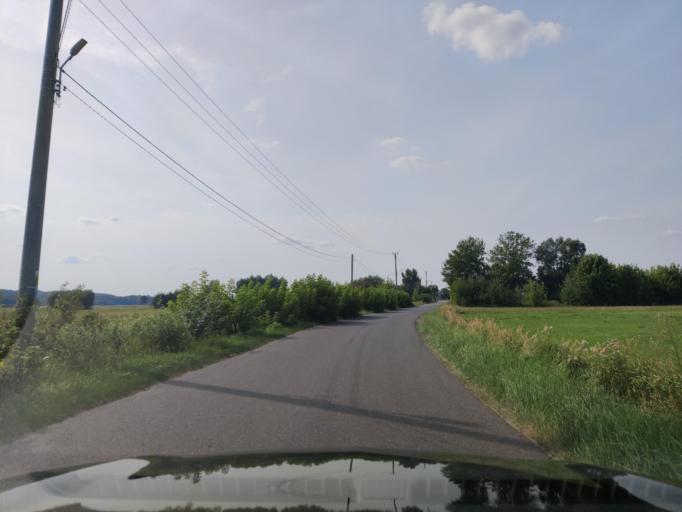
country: PL
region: Masovian Voivodeship
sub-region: Powiat wyszkowski
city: Rzasnik
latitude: 52.7379
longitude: 21.3441
